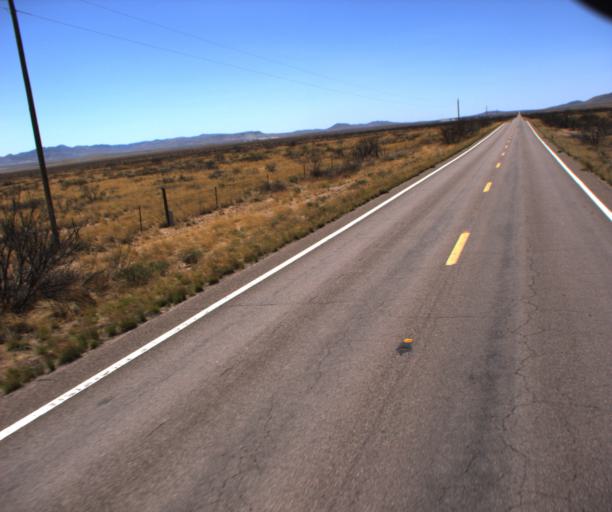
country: US
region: Arizona
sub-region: Cochise County
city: Douglas
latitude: 31.7478
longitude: -109.0931
